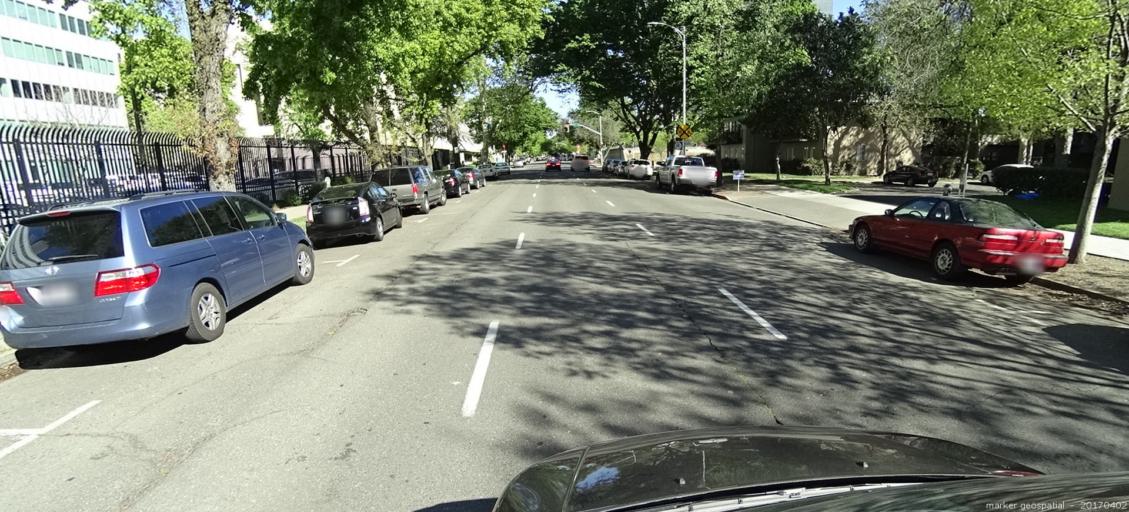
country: US
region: California
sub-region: Sacramento County
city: Sacramento
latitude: 38.5772
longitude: -121.5003
